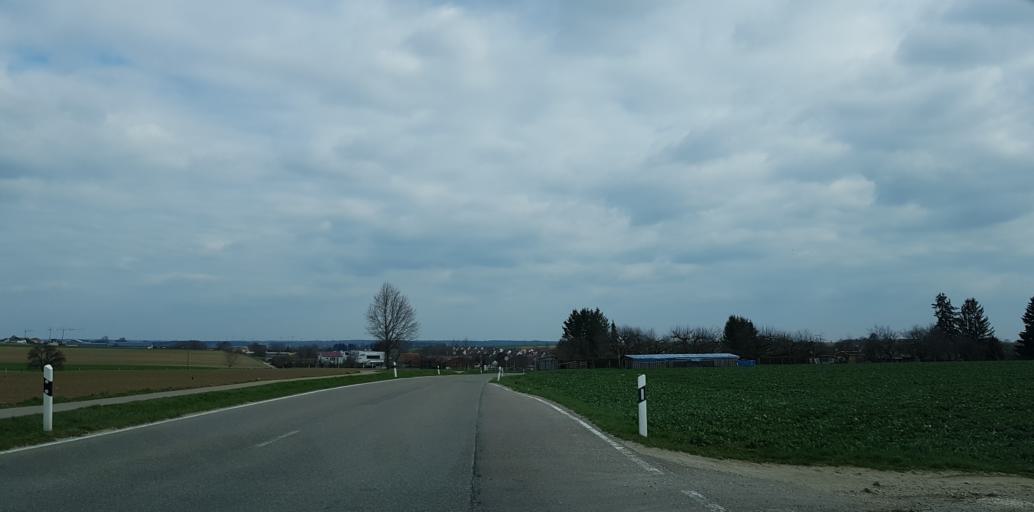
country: DE
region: Baden-Wuerttemberg
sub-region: Tuebingen Region
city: Erbach
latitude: 48.3582
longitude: 9.8904
